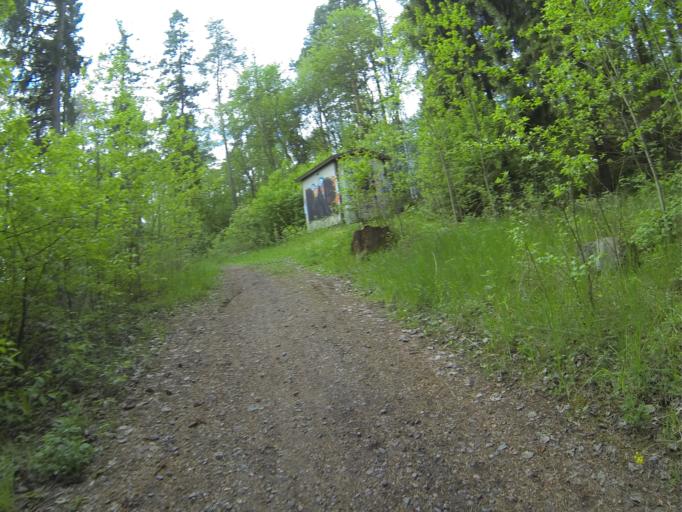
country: FI
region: Varsinais-Suomi
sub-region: Salo
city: Salo
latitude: 60.3719
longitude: 23.1191
